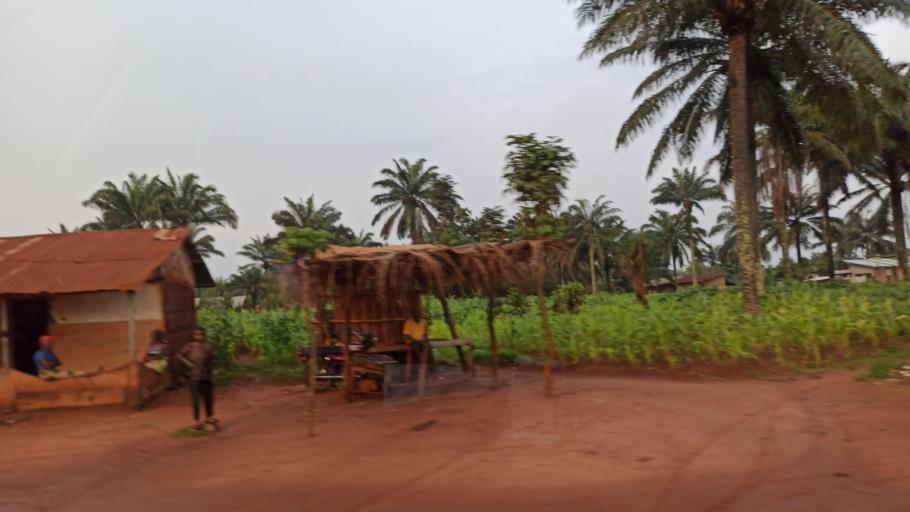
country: BJ
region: Queme
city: Porto-Novo
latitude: 6.5468
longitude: 2.6138
